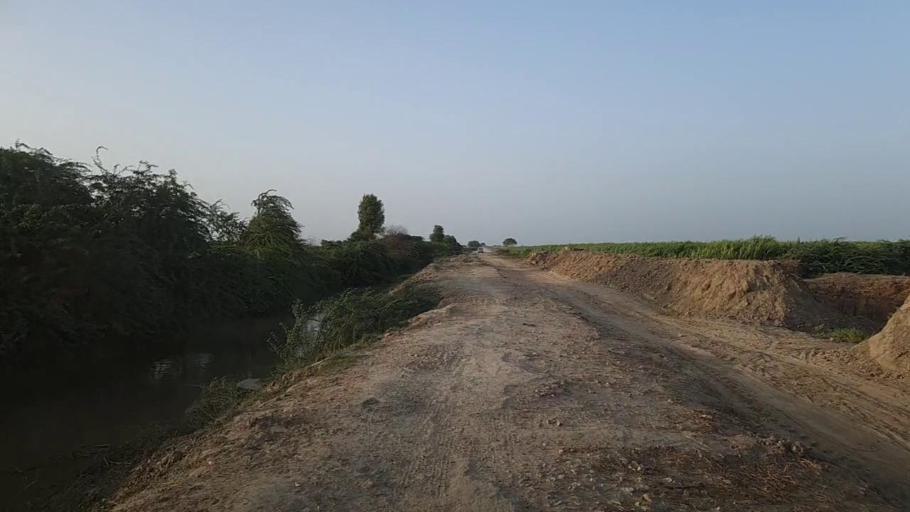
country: PK
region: Sindh
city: Kario
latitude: 24.7039
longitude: 68.4649
